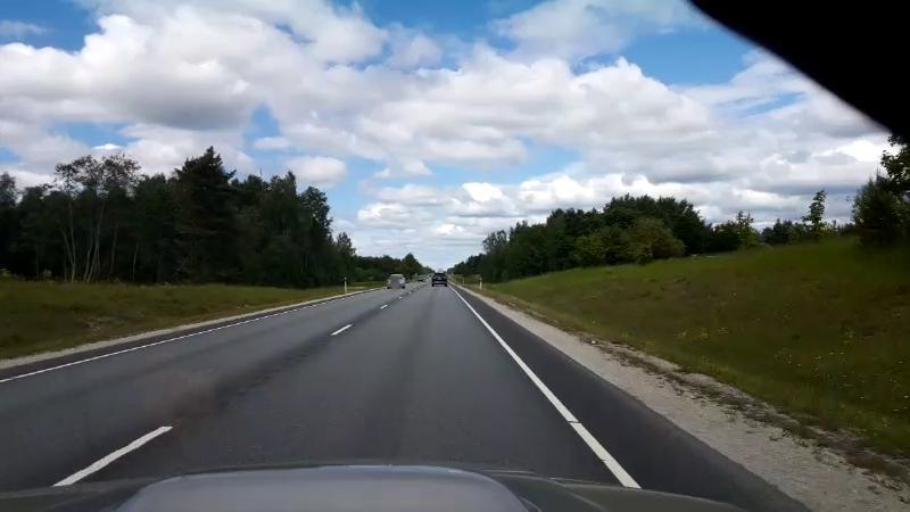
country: EE
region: Harju
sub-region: Nissi vald
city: Riisipere
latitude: 59.0553
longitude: 24.4466
